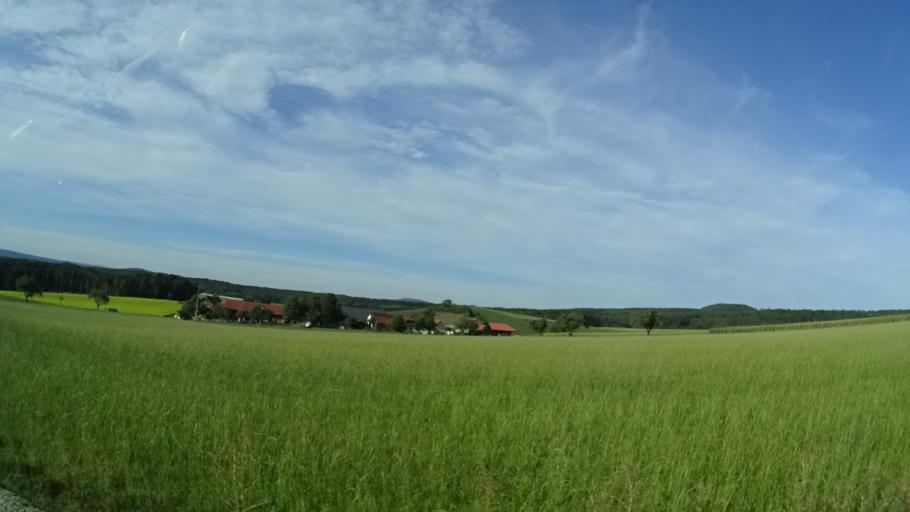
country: DE
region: Hesse
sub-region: Regierungsbezirk Kassel
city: Dipperz
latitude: 50.5384
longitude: 9.8208
